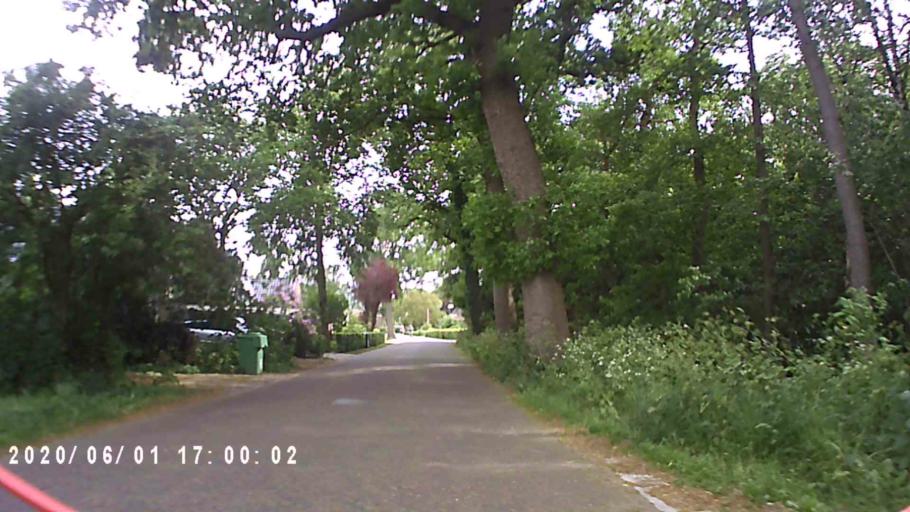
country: NL
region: Friesland
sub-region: Gemeente Tytsjerksteradiel
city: Hurdegaryp
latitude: 53.1842
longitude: 5.9290
